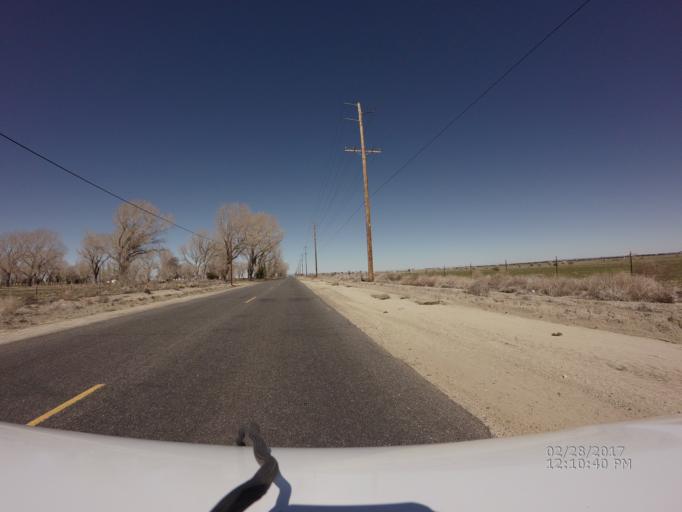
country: US
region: California
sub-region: Los Angeles County
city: Palmdale
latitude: 34.5978
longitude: -118.0585
